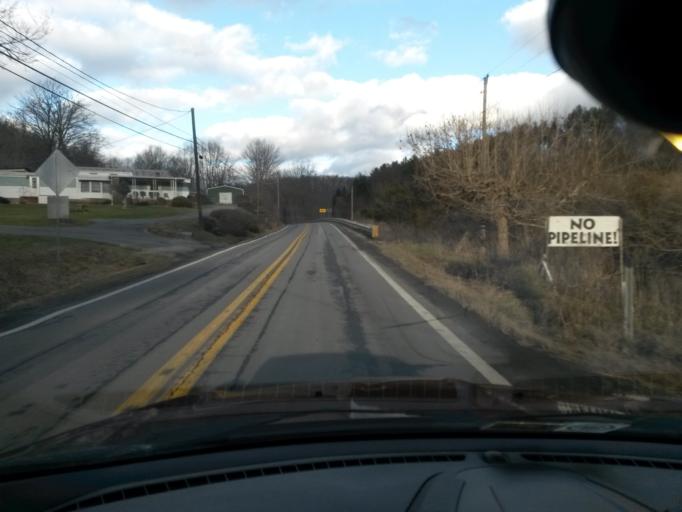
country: US
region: West Virginia
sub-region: Monroe County
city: Union
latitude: 37.5711
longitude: -80.5709
